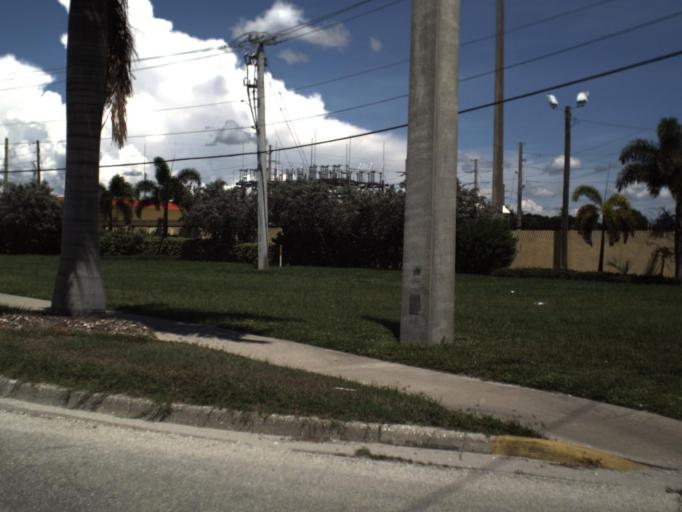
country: US
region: Florida
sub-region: Charlotte County
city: Punta Gorda
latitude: 26.9331
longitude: -82.0474
